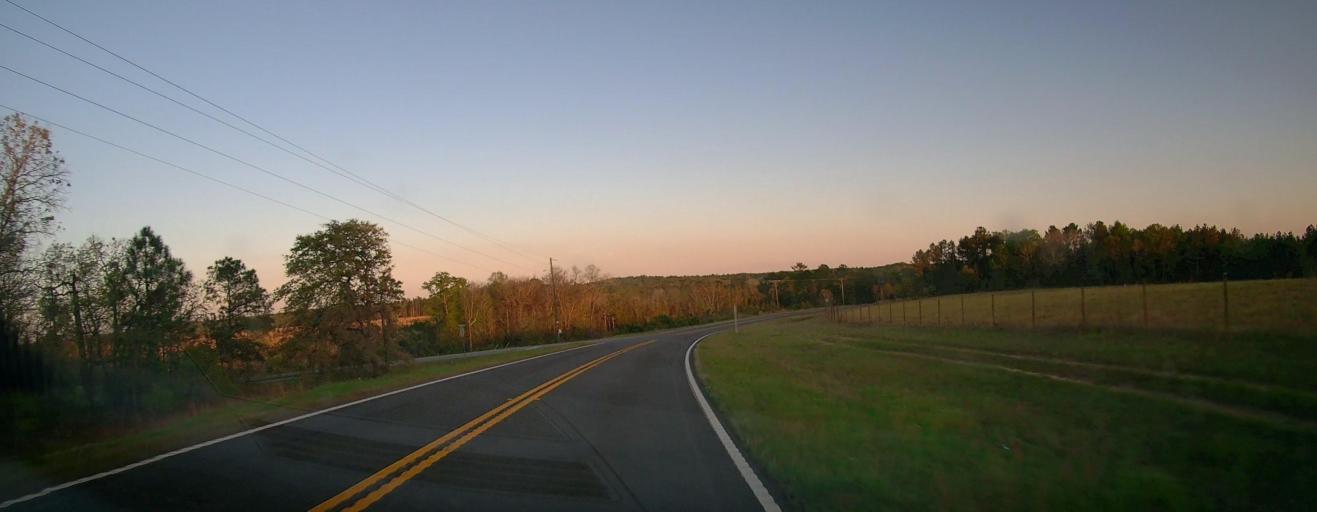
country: US
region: Georgia
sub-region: Marion County
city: Buena Vista
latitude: 32.4396
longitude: -84.6012
